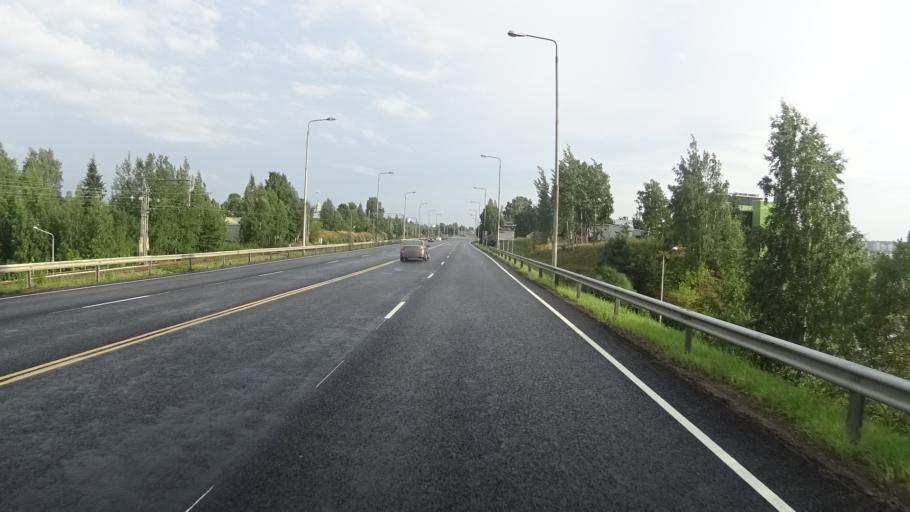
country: FI
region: Kymenlaakso
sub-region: Kotka-Hamina
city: Kotka
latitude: 60.4706
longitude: 26.9184
